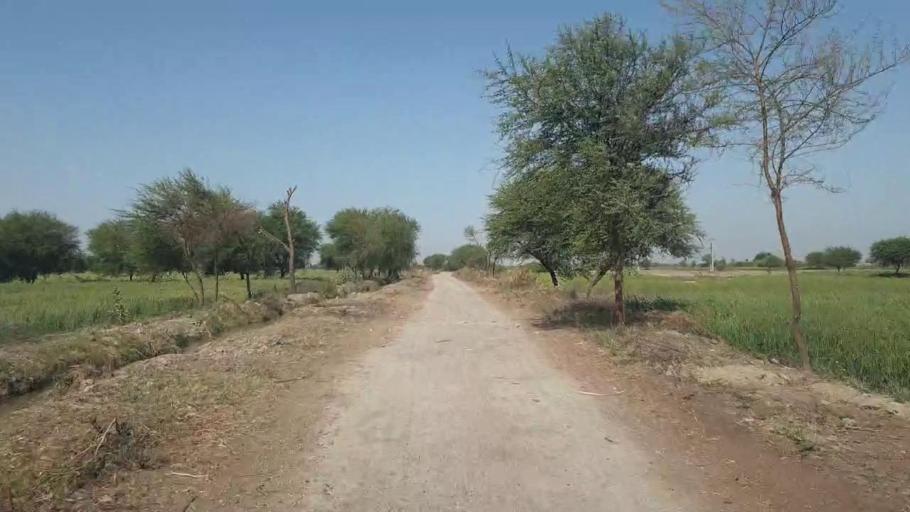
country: PK
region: Sindh
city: Umarkot
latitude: 25.2972
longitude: 69.6258
